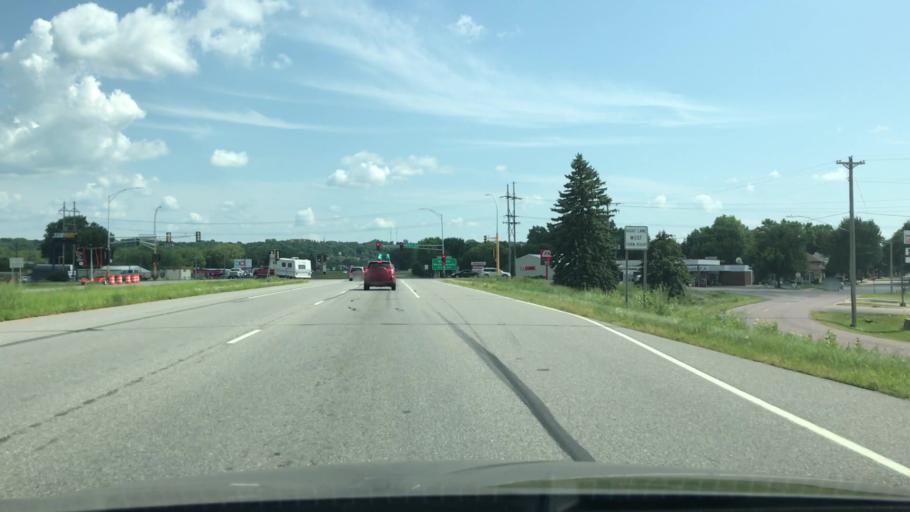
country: US
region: Minnesota
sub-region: Blue Earth County
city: Mankato
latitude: 44.1823
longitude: -94.0088
